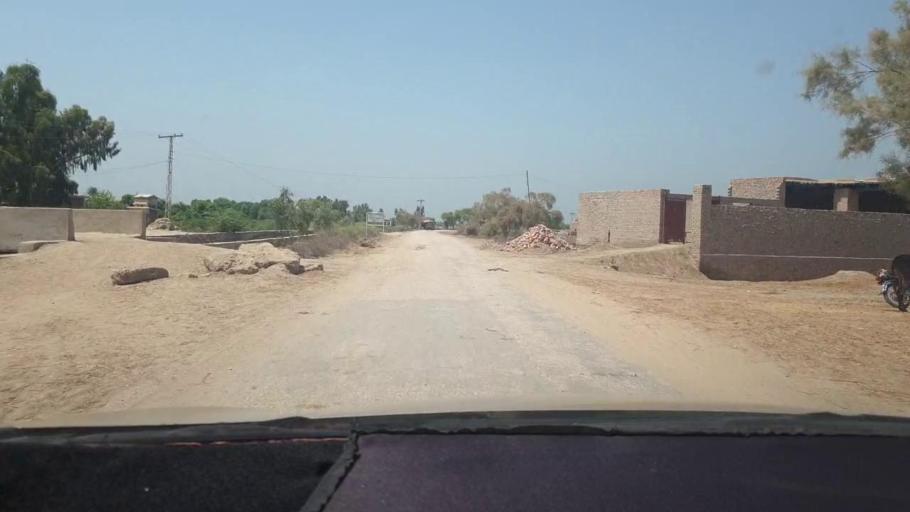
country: PK
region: Sindh
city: Miro Khan
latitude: 27.6695
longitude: 68.0617
